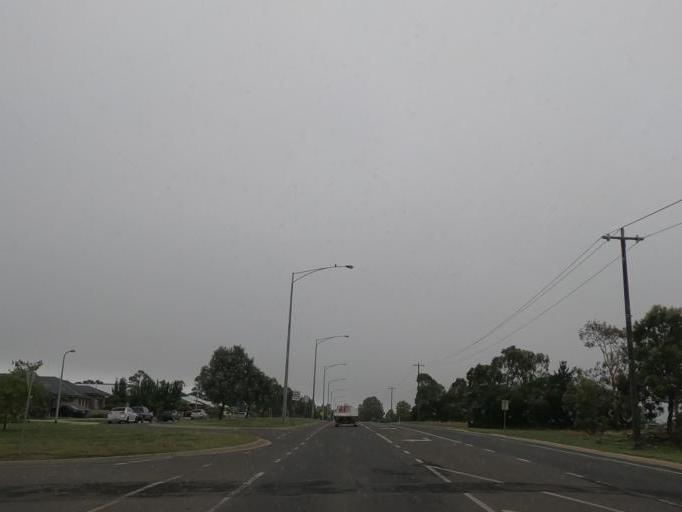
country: AU
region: Victoria
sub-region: Ballarat North
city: Newington
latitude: -37.5614
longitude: 143.8120
